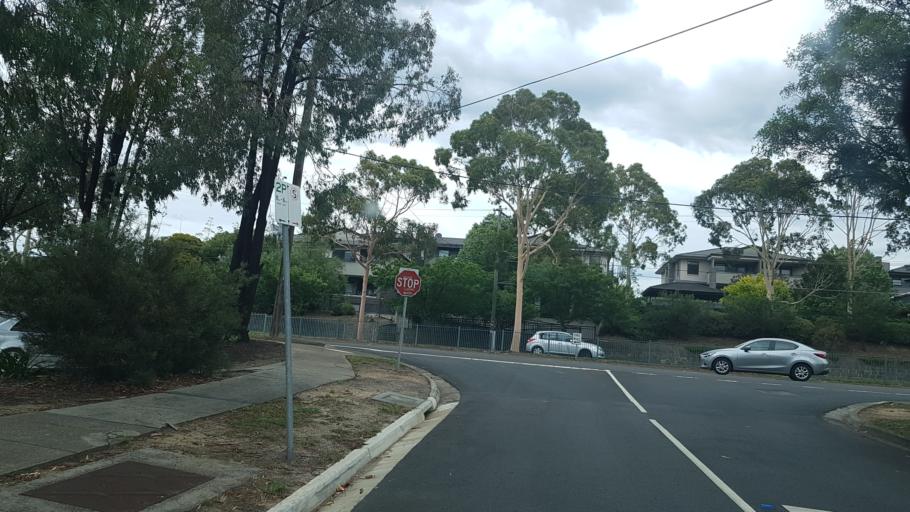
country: AU
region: Victoria
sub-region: Manningham
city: Bulleen
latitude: -37.7660
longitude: 145.0909
